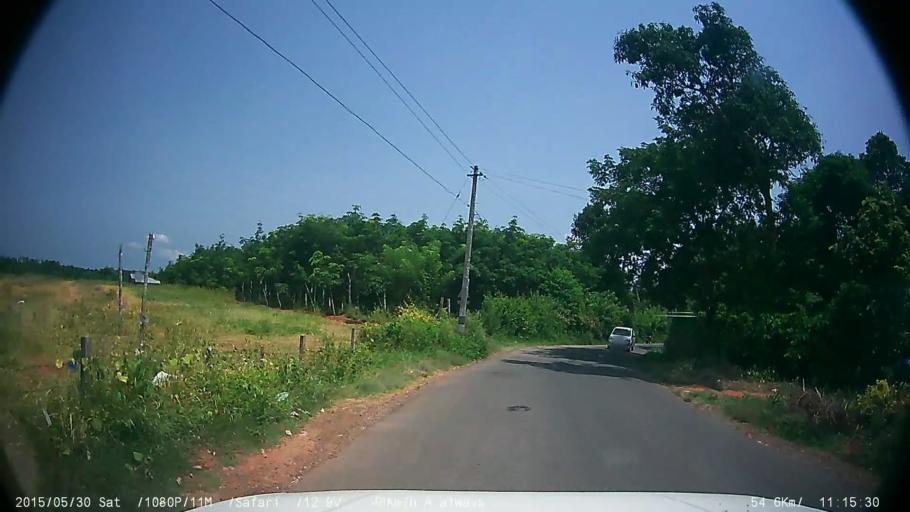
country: IN
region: Kerala
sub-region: Wayanad
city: Panamaram
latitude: 11.7712
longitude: 76.0605
